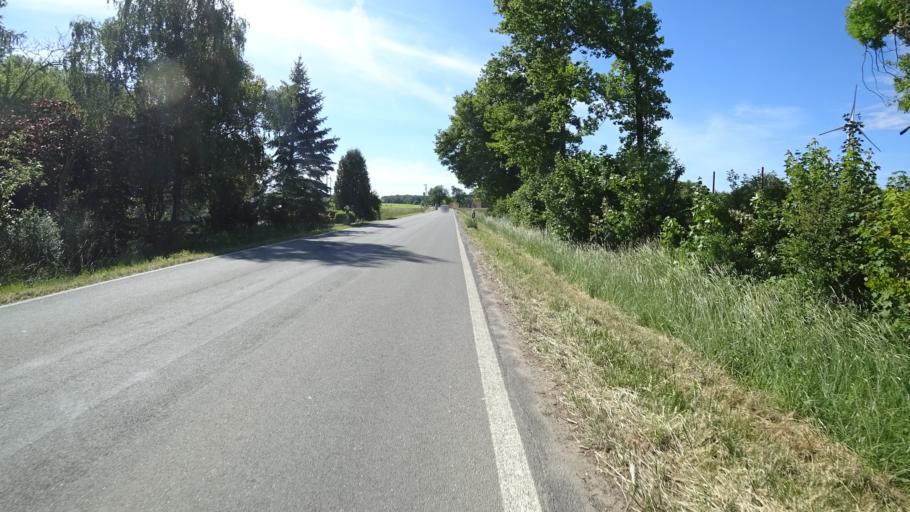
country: DE
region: North Rhine-Westphalia
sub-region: Regierungsbezirk Detmold
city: Rheda-Wiedenbruck
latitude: 51.8238
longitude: 8.2420
